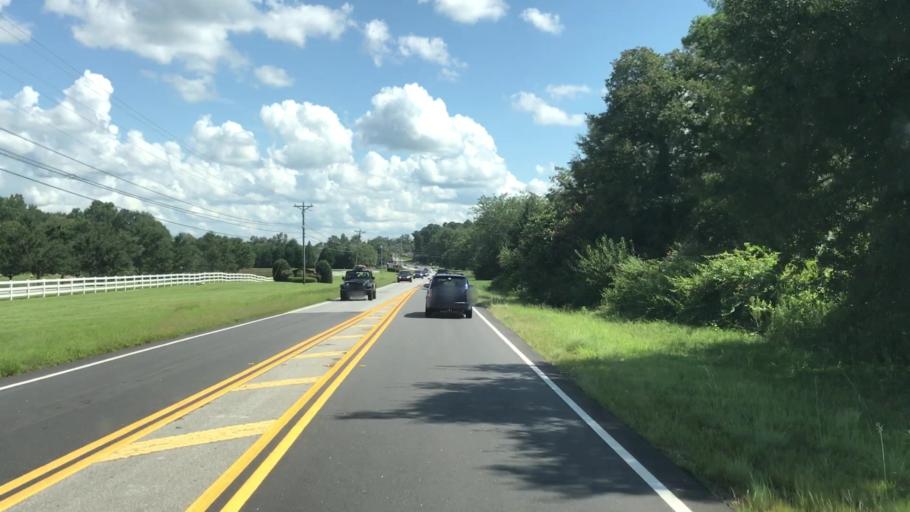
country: US
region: Georgia
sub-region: Walton County
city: Loganville
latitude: 33.8247
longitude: -83.8782
